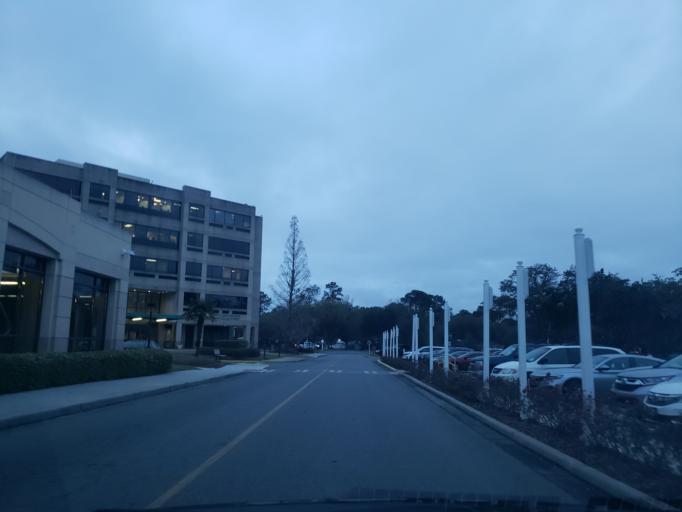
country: US
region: Georgia
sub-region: Chatham County
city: Thunderbolt
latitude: 32.0279
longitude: -81.1006
